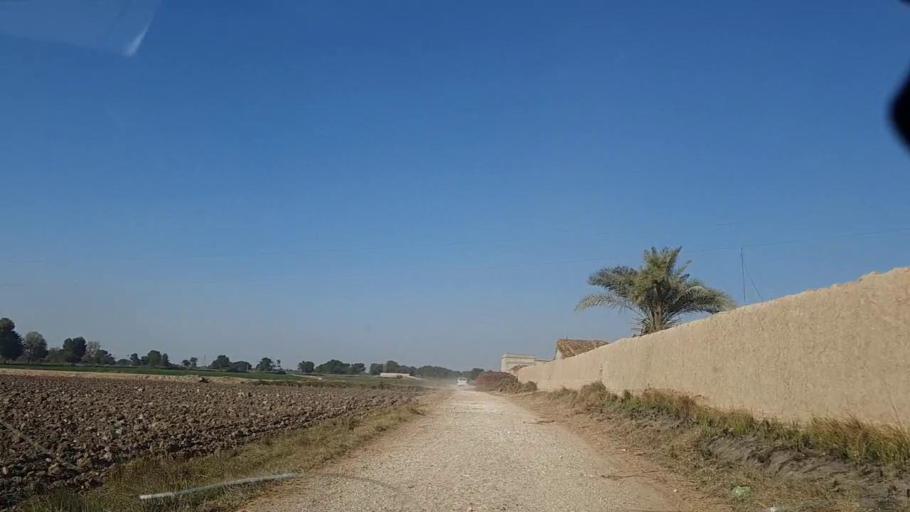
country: PK
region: Sindh
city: Khanpur
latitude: 27.7847
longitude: 69.3521
